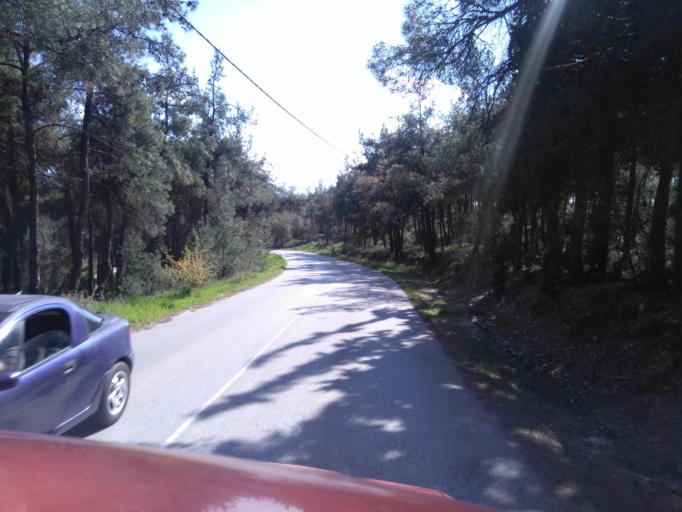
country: GR
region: Central Macedonia
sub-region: Nomos Thessalonikis
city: Pefka
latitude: 40.6439
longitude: 22.9822
